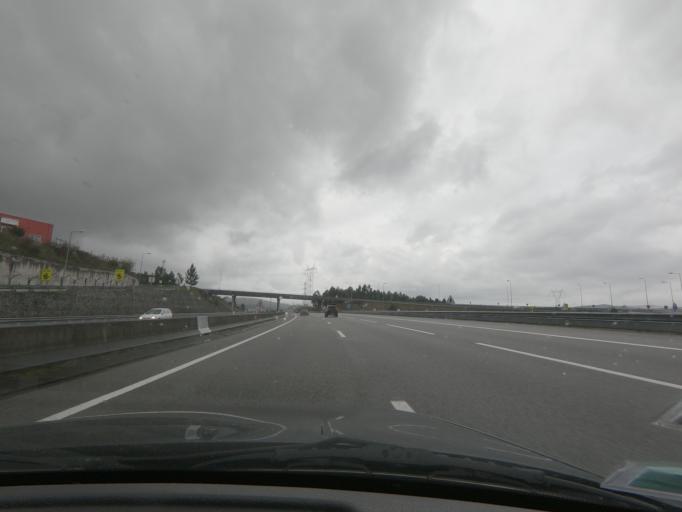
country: PT
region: Porto
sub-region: Valongo
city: Campo
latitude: 41.1788
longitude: -8.4432
